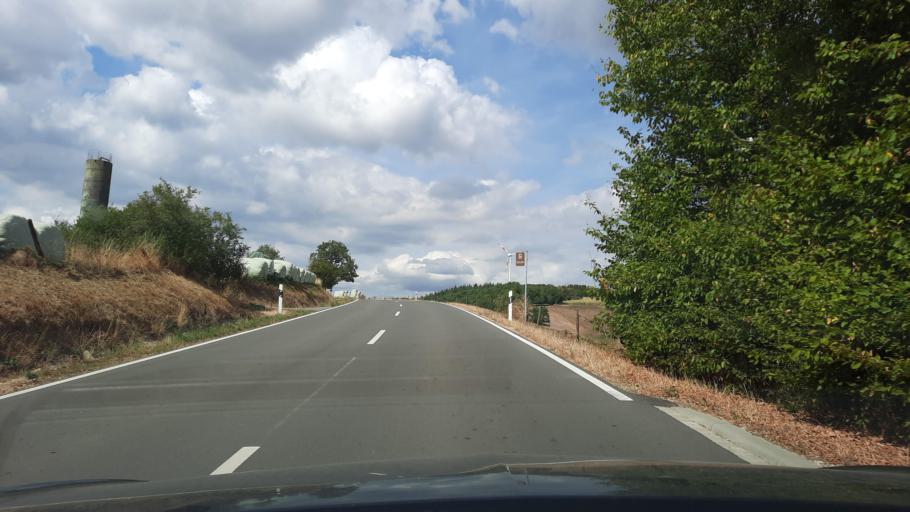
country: DE
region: Rheinland-Pfalz
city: Pronsfeld
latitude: 50.1626
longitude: 6.3301
